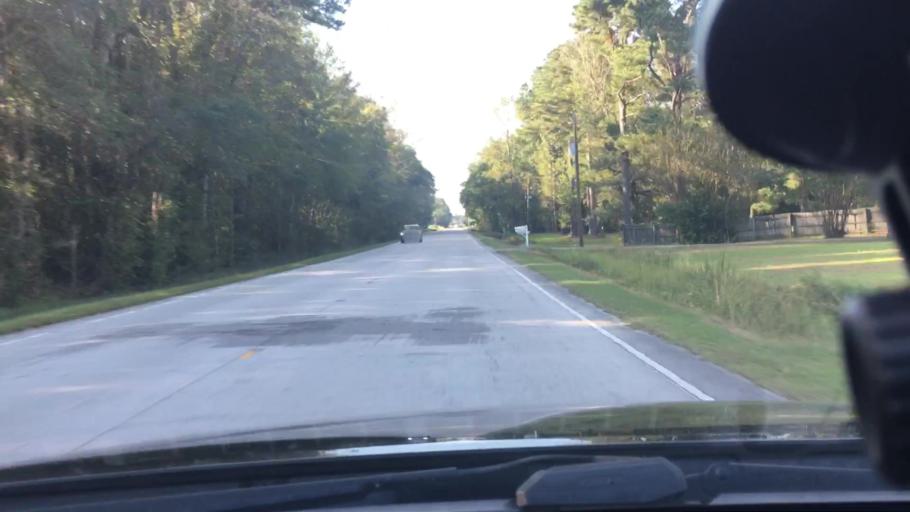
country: US
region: North Carolina
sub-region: Craven County
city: Vanceboro
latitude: 35.3897
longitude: -77.2299
